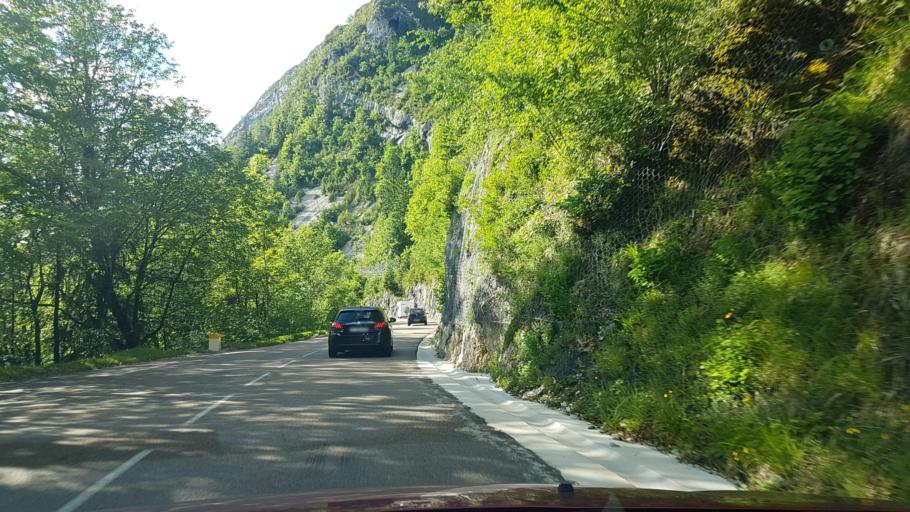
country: FR
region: Franche-Comte
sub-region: Departement du Jura
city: Saint-Claude
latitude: 46.3579
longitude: 5.9015
